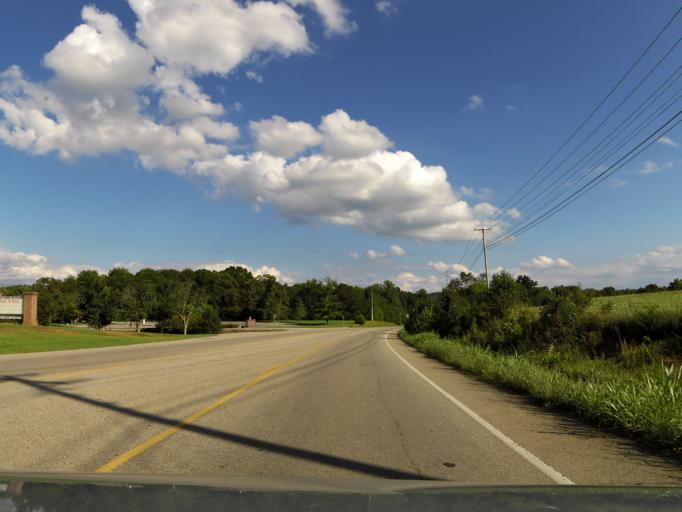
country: US
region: Tennessee
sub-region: Blount County
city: Maryville
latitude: 35.7387
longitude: -84.0369
